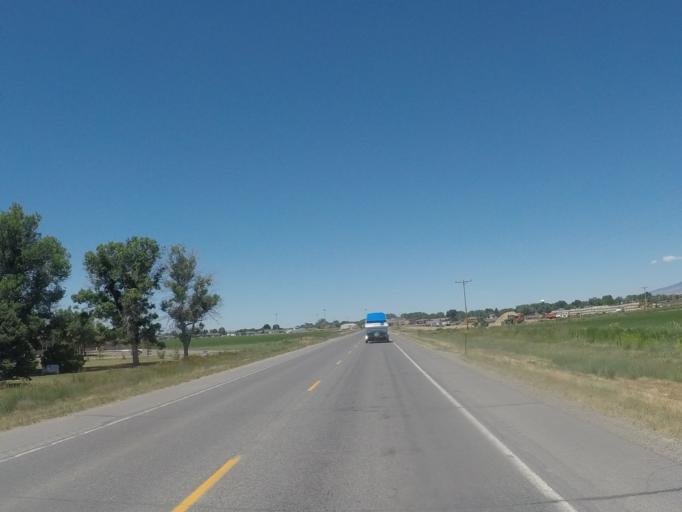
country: US
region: Wyoming
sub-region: Big Horn County
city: Lovell
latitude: 44.8703
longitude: -108.4567
